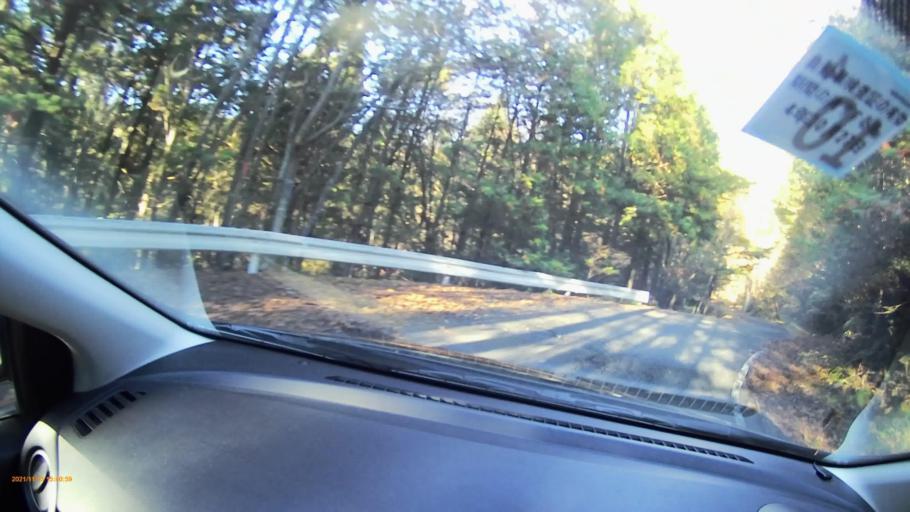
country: JP
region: Gifu
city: Nakatsugawa
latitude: 35.5859
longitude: 137.3887
